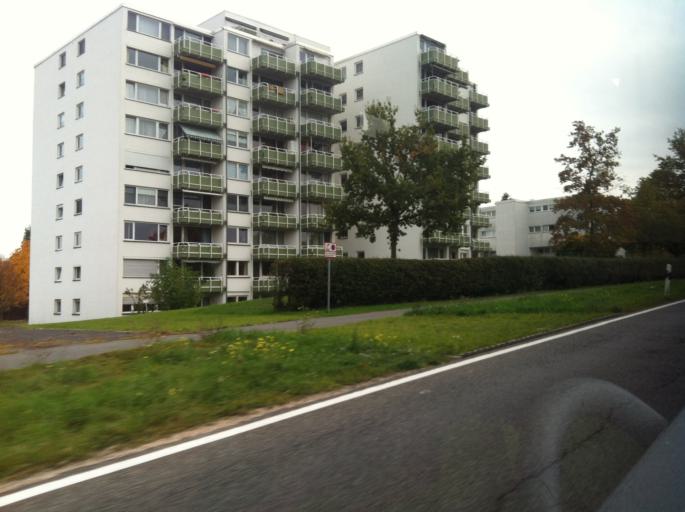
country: DE
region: Rheinland-Pfalz
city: Ober-Olm
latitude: 49.9675
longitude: 8.1868
